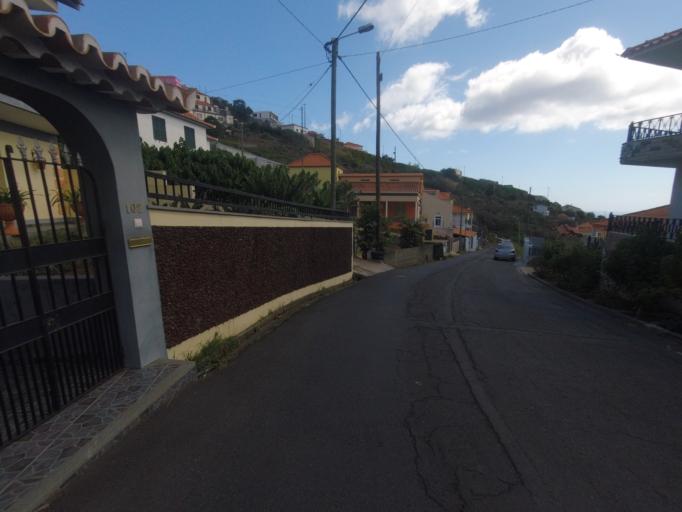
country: PT
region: Madeira
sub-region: Ribeira Brava
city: Campanario
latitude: 32.6727
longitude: -17.0481
